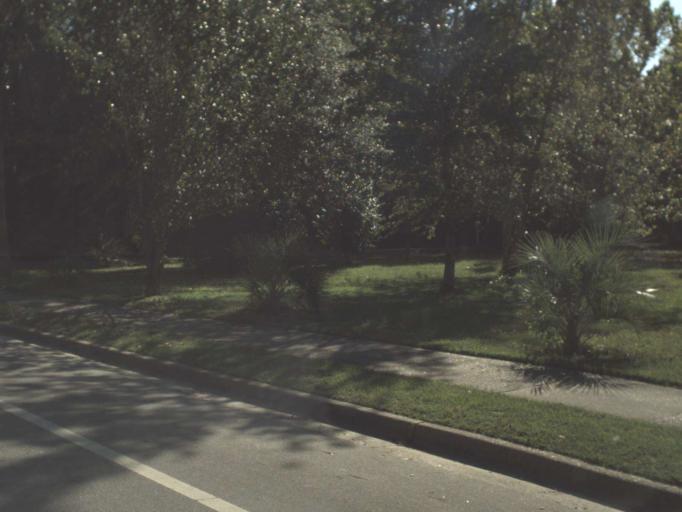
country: US
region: Florida
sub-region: Gulf County
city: Wewahitchka
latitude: 30.1085
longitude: -85.2005
